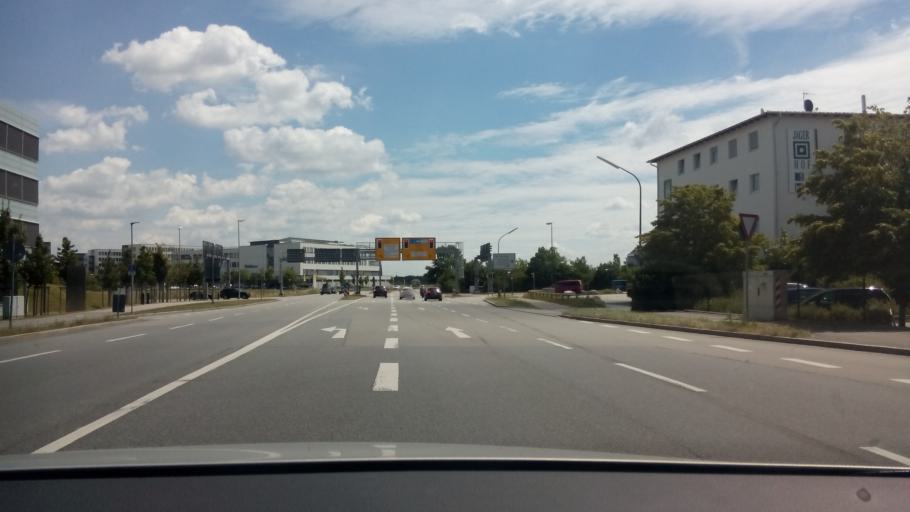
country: DE
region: Bavaria
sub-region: Upper Bavaria
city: Garching bei Munchen
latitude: 48.2495
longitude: 11.6290
